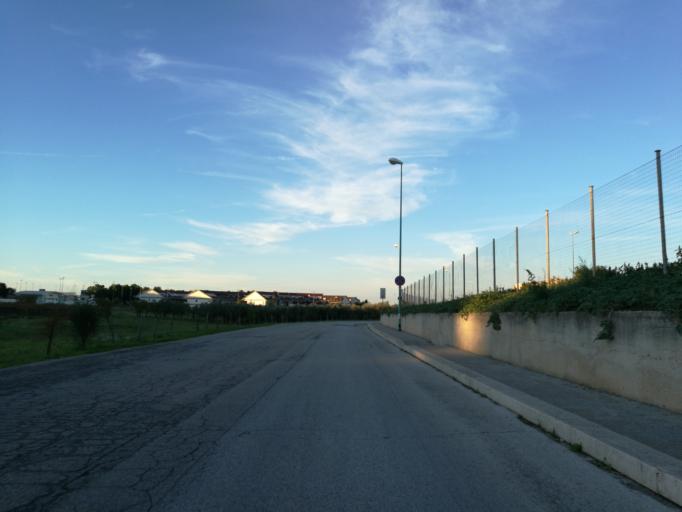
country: IT
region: Apulia
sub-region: Provincia di Bari
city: Adelfia
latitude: 41.0045
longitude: 16.8740
